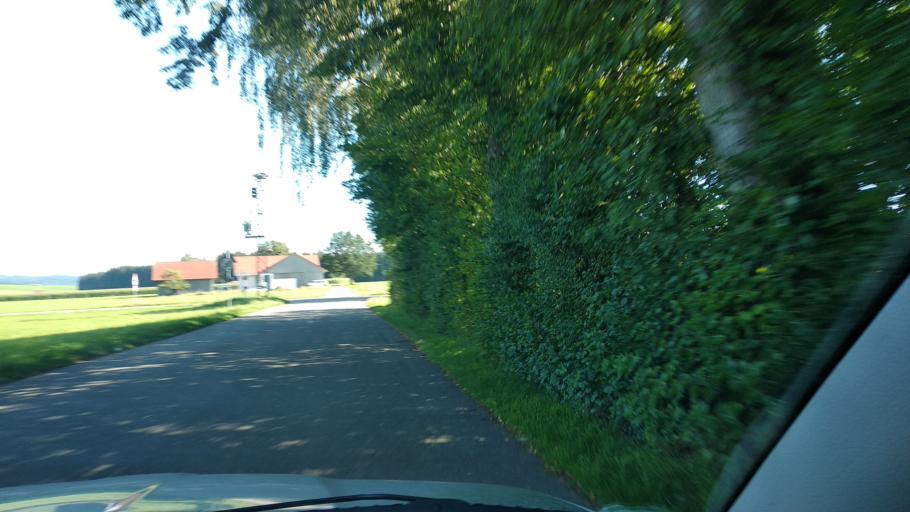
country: DE
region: Baden-Wuerttemberg
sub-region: Tuebingen Region
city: Leutkirch im Allgau
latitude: 47.8104
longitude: 10.0634
